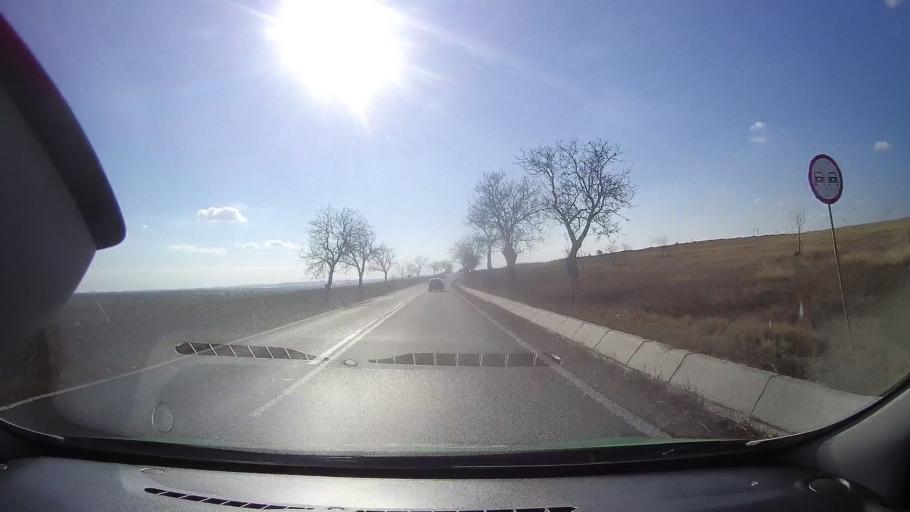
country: RO
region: Tulcea
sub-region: Comuna Ceamurlia de Jos
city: Ceamurlia de Jos
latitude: 44.8090
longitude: 28.6913
